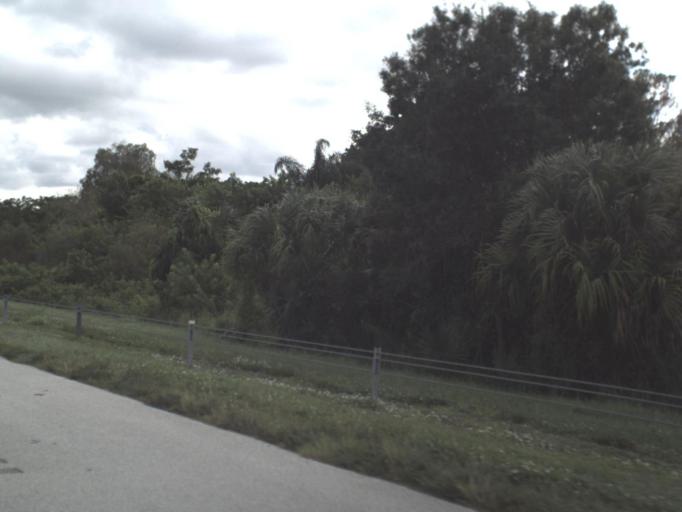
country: US
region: Florida
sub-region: Martin County
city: Palm City
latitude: 27.1089
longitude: -80.2690
